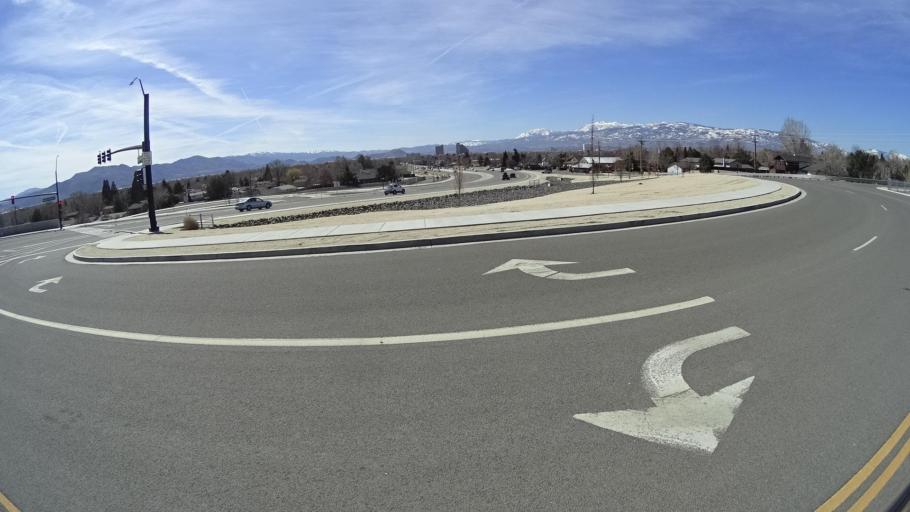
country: US
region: Nevada
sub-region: Washoe County
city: Sparks
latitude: 39.5622
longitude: -119.7514
